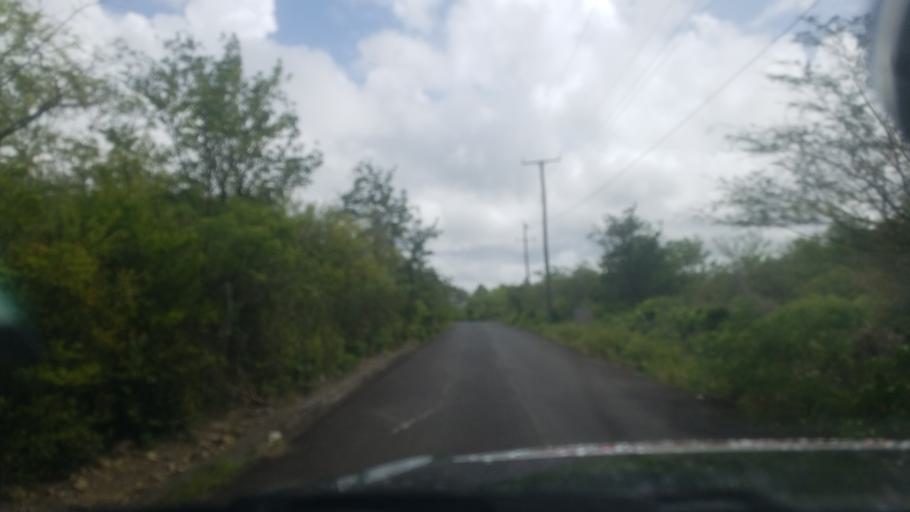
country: LC
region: Laborie Quarter
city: Laborie
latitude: 13.7393
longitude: -60.9757
